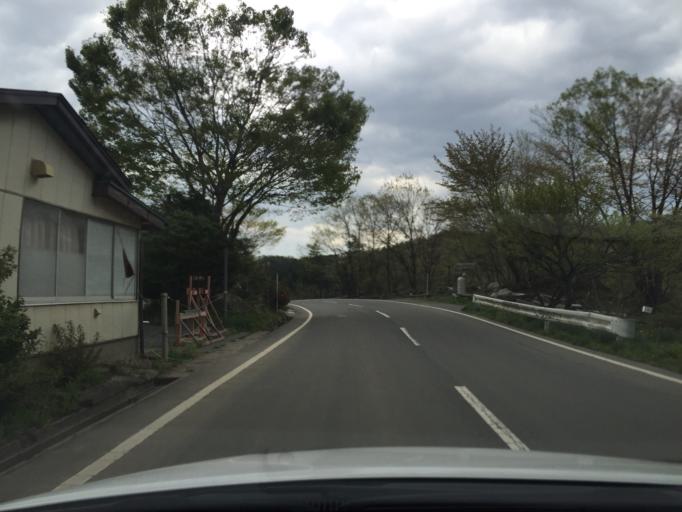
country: JP
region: Fukushima
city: Yanagawamachi-saiwaicho
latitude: 37.7104
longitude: 140.7387
